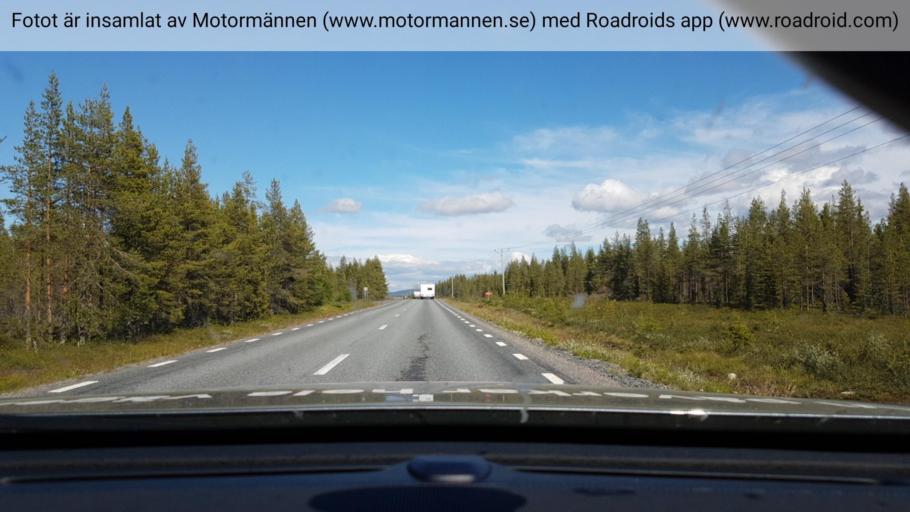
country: SE
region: Norrbotten
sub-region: Arjeplogs Kommun
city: Arjeplog
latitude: 65.5791
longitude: 18.0893
